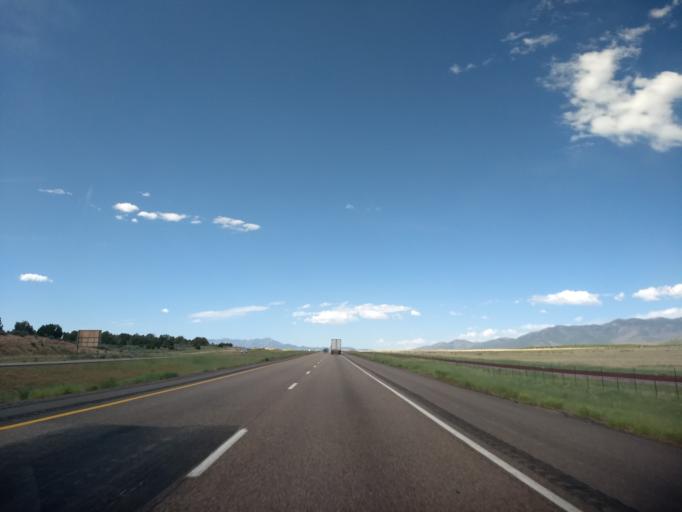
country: US
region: Utah
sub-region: Millard County
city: Fillmore
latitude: 39.0129
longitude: -112.3080
